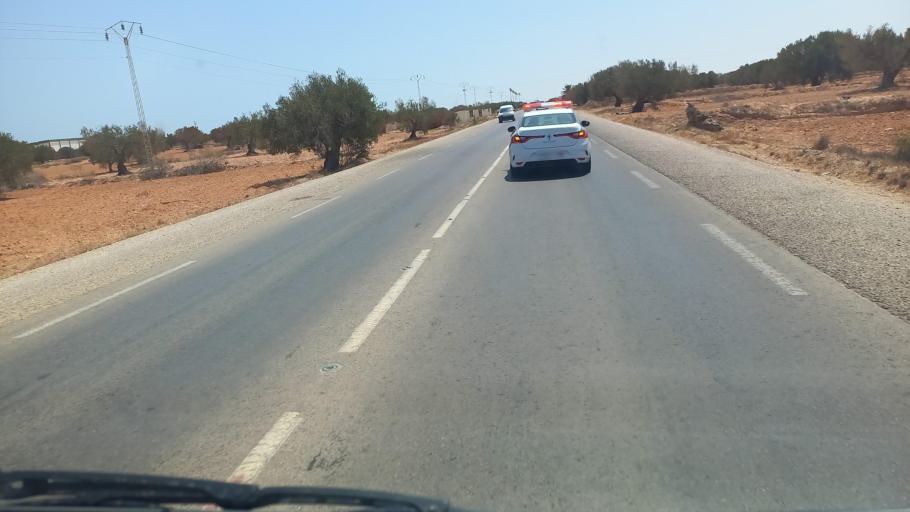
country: TN
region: Madanin
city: Zarzis
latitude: 33.5595
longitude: 11.0562
